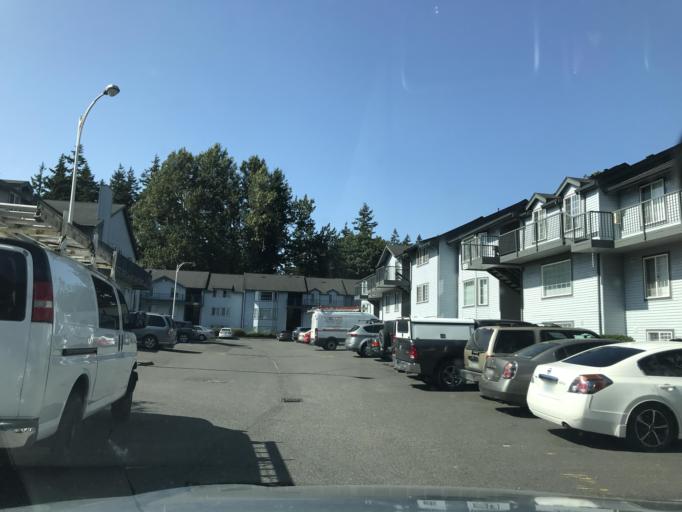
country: US
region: Washington
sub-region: Whatcom County
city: Bellingham
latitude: 48.7761
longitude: -122.4914
